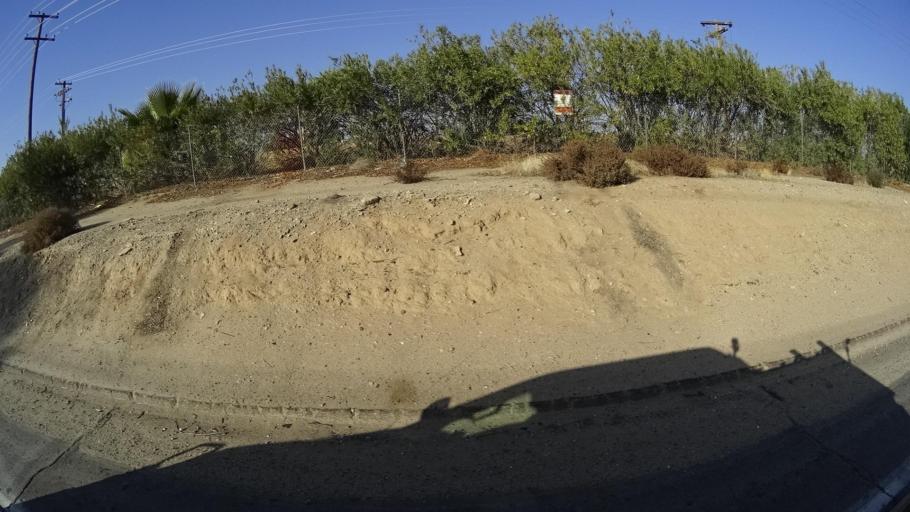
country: US
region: California
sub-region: Kern County
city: Oildale
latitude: 35.4269
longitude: -119.0015
